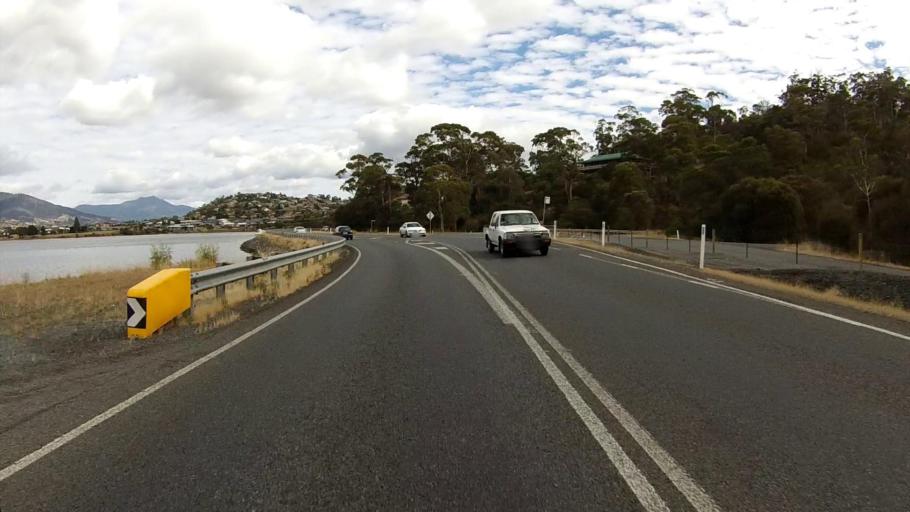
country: AU
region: Tasmania
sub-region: Brighton
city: Old Beach
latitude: -42.7838
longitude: 147.2877
